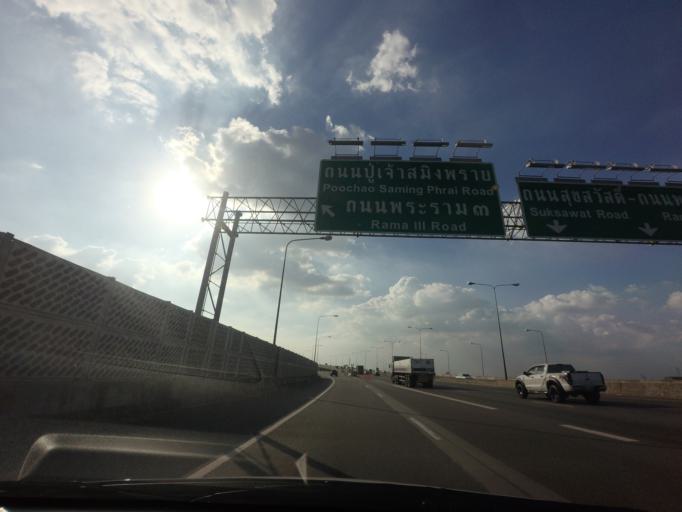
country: TH
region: Samut Prakan
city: Phra Pradaeng
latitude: 13.6386
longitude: 100.5549
